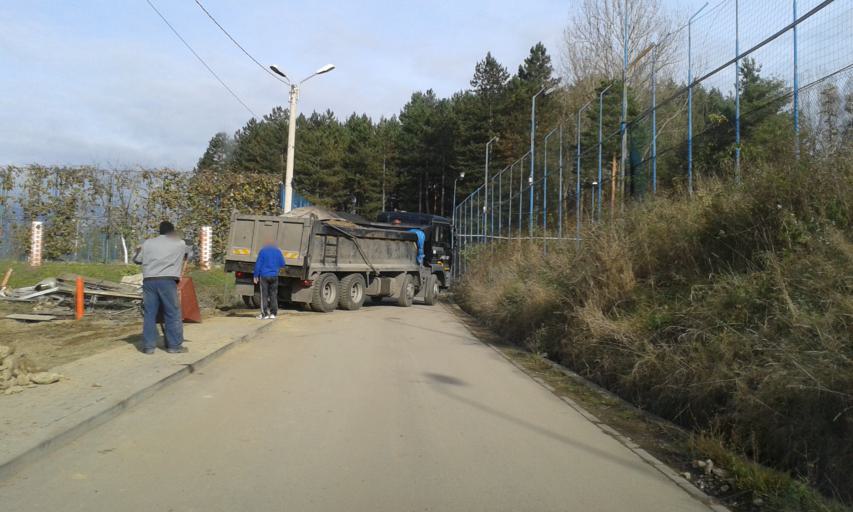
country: RO
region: Hunedoara
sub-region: Municipiul Petrosani
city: Petrosani
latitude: 45.4212
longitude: 23.3793
